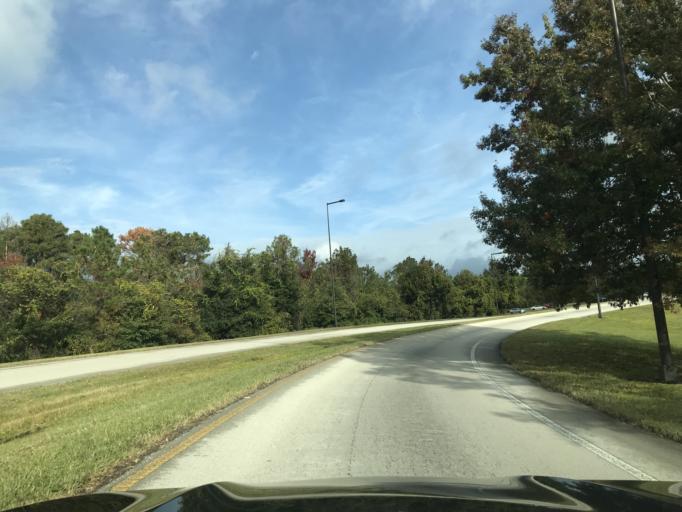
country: US
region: Florida
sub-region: Osceola County
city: Celebration
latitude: 28.3617
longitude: -81.5666
